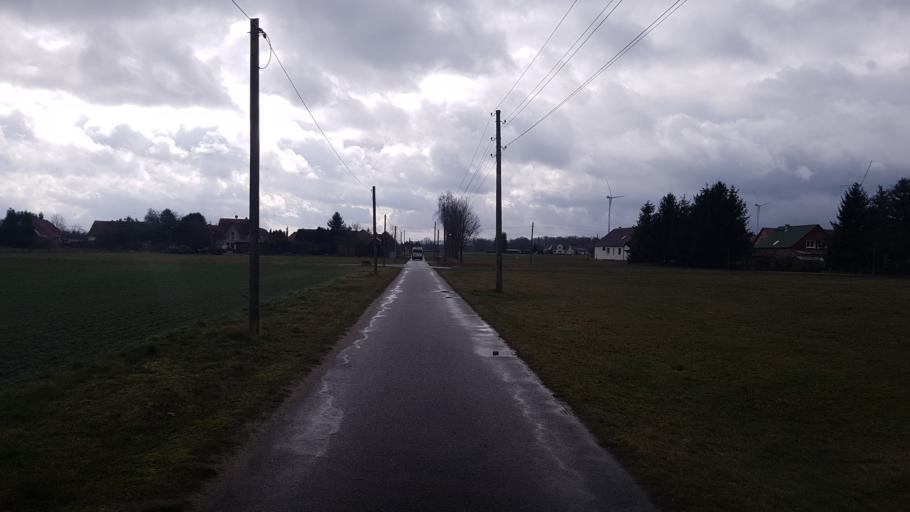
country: DE
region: Brandenburg
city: Sallgast
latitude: 51.6432
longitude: 13.8531
